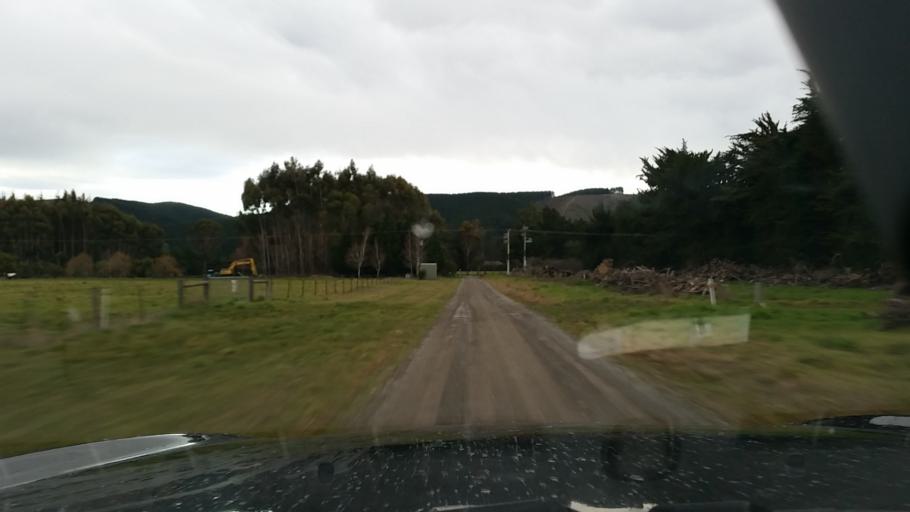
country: NZ
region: Nelson
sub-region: Nelson City
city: Nelson
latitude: -41.5644
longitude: 173.5236
